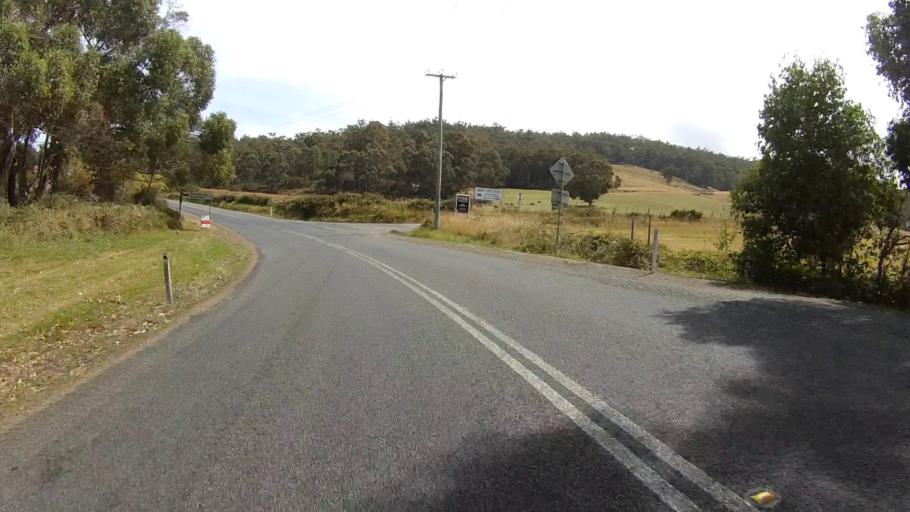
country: AU
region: Tasmania
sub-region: Huon Valley
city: Cygnet
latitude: -43.1849
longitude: 147.1073
